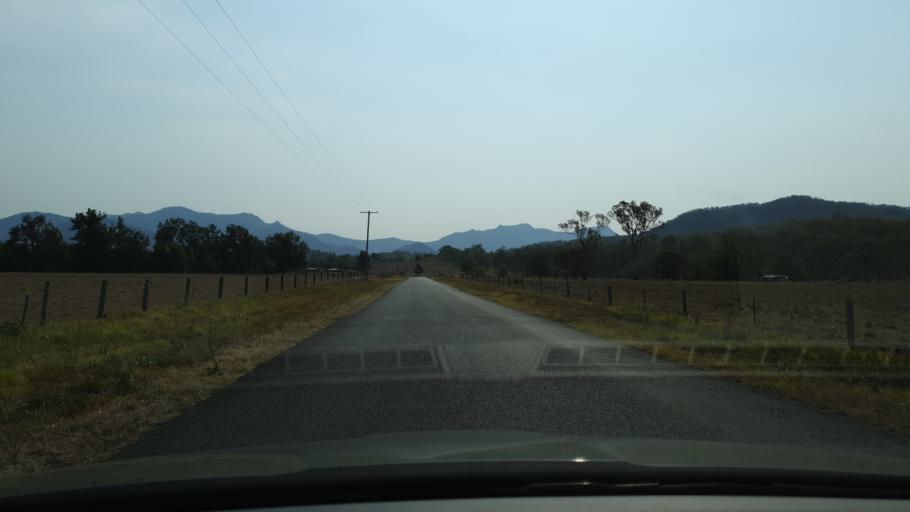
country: AU
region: Queensland
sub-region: Ipswich
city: Deebing Heights
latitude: -28.1381
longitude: 152.5764
